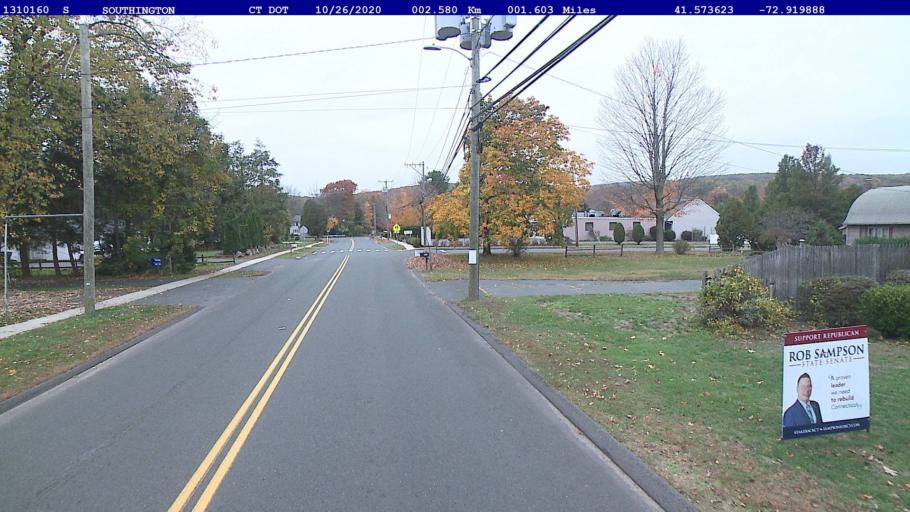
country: US
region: Connecticut
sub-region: New Haven County
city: Wolcott
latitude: 41.5736
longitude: -72.9199
